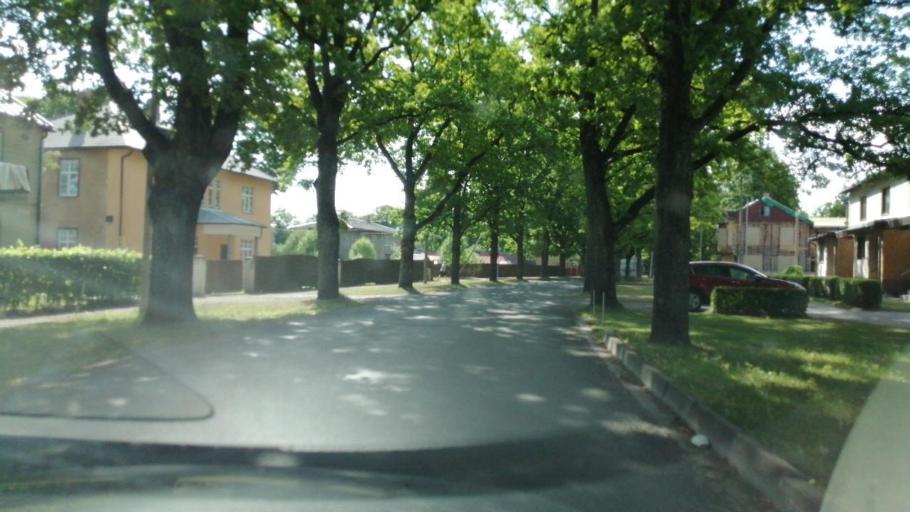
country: EE
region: Viljandimaa
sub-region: Viljandi linn
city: Viljandi
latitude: 58.3700
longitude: 25.6018
